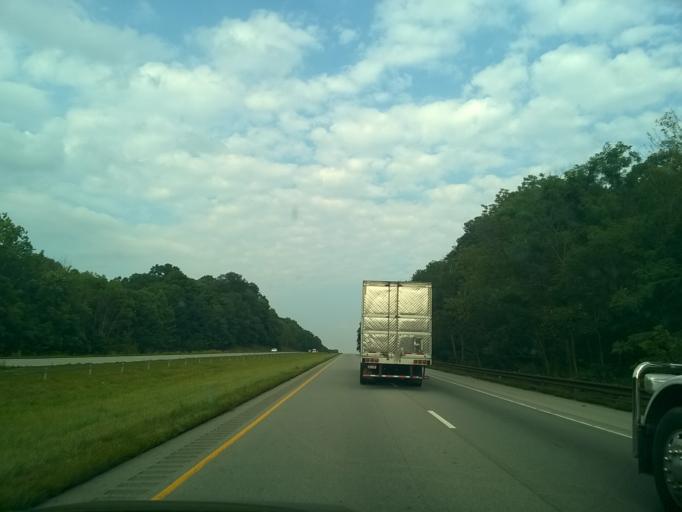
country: US
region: Indiana
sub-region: Putnam County
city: Cloverdale
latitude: 39.5087
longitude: -86.9380
